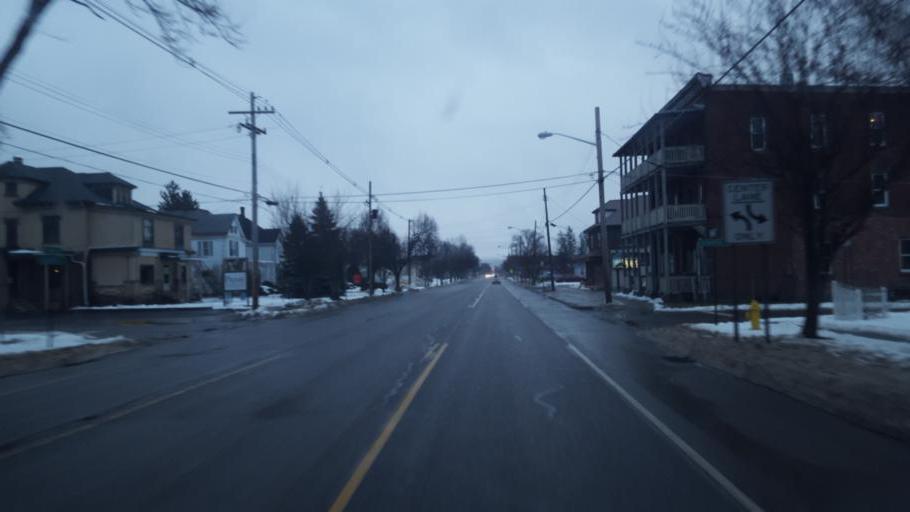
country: US
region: New York
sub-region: Chautauqua County
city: Falconer
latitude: 42.1151
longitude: -79.2023
